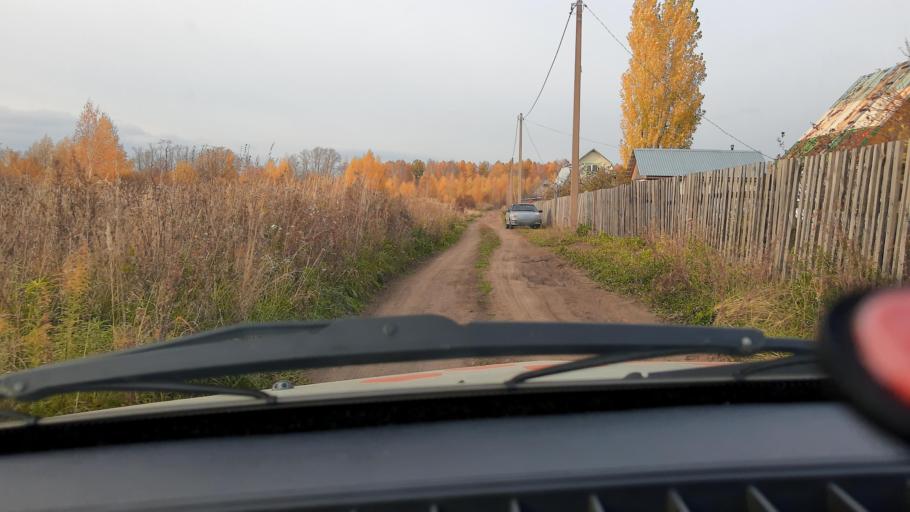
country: RU
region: Bashkortostan
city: Iglino
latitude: 54.8038
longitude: 56.3479
